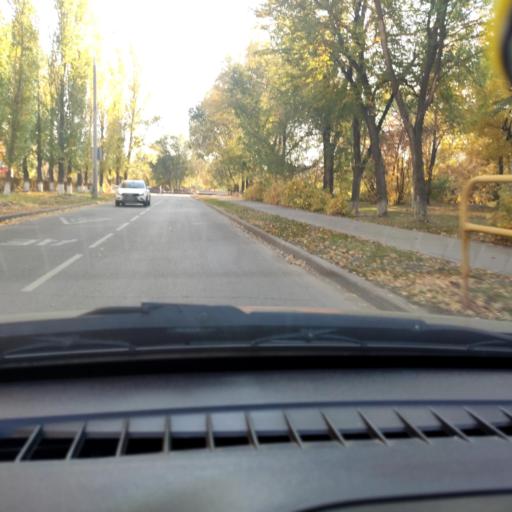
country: RU
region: Samara
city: Tol'yatti
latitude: 53.5222
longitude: 49.2697
